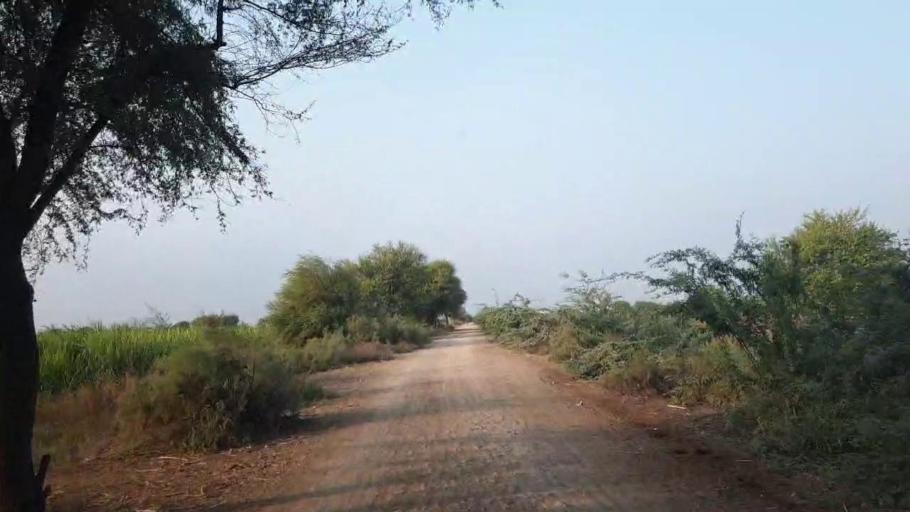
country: PK
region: Sindh
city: Tando Ghulam Ali
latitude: 25.0528
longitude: 68.9605
